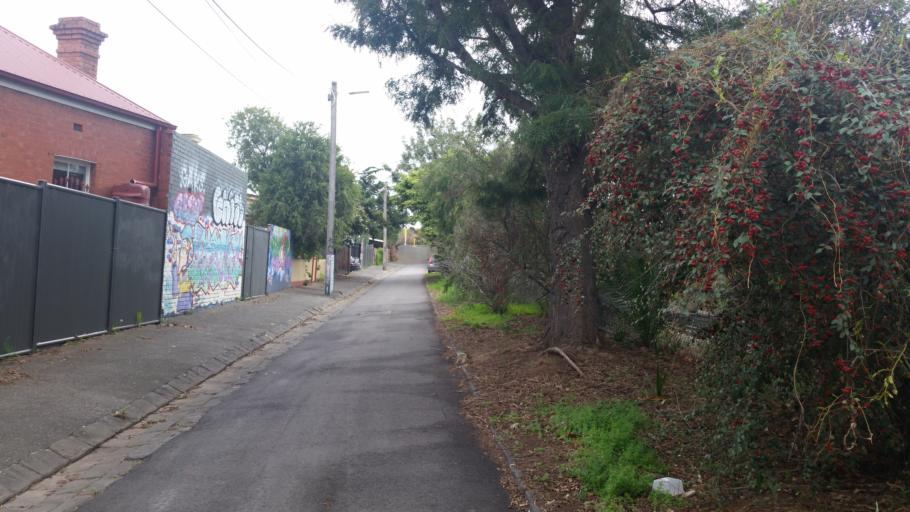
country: AU
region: Victoria
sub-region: Moonee Valley
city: Moonee Ponds
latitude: -37.7732
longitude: 144.9208
